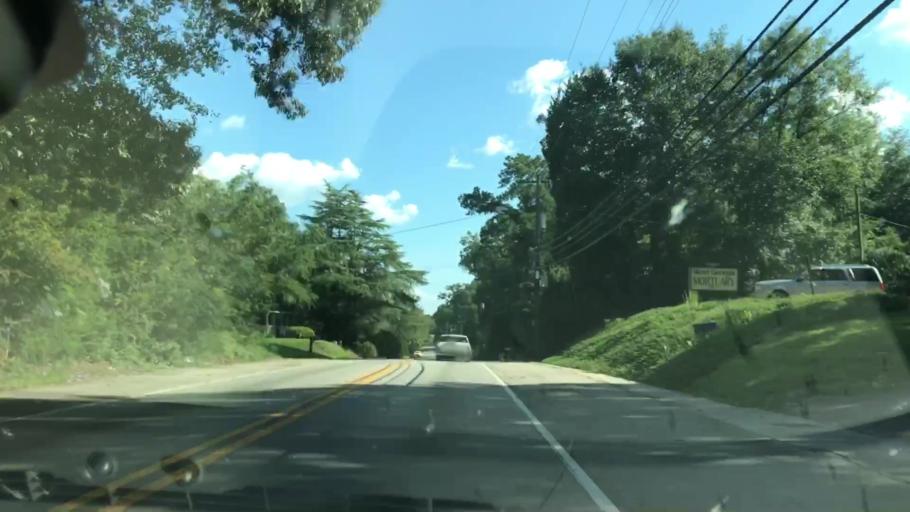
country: US
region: Georgia
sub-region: Troup County
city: La Grange
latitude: 33.0199
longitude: -85.0230
